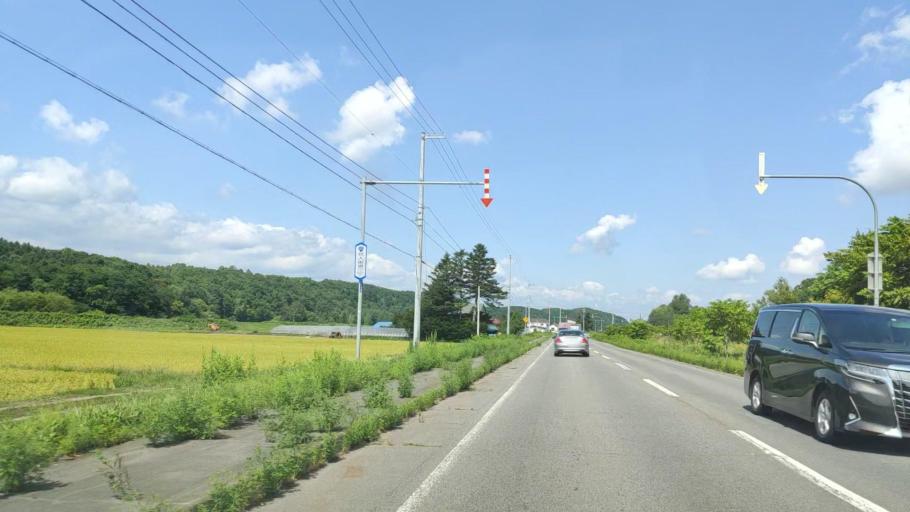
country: JP
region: Hokkaido
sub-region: Asahikawa-shi
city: Asahikawa
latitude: 43.6307
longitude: 142.4609
